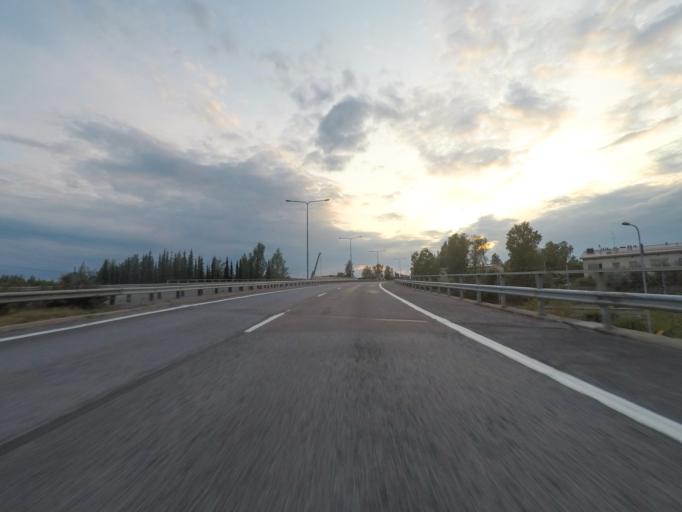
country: FI
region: Central Finland
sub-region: Jyvaeskylae
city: Jyvaeskylae
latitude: 62.2465
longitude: 25.7675
